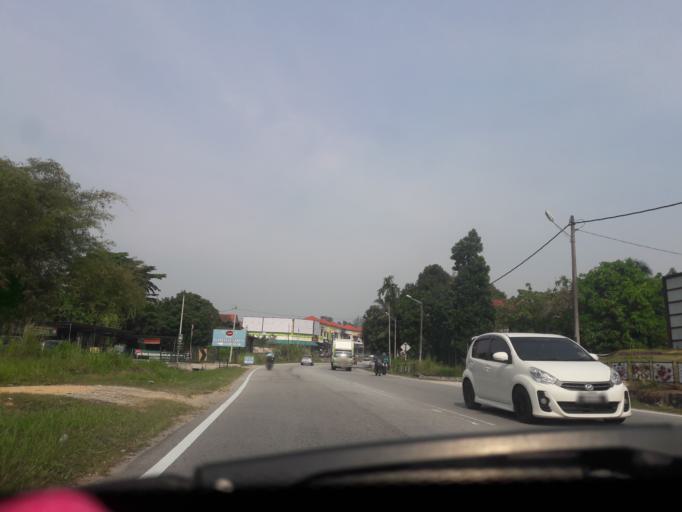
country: MY
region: Kedah
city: Kulim
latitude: 5.3670
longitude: 100.5485
